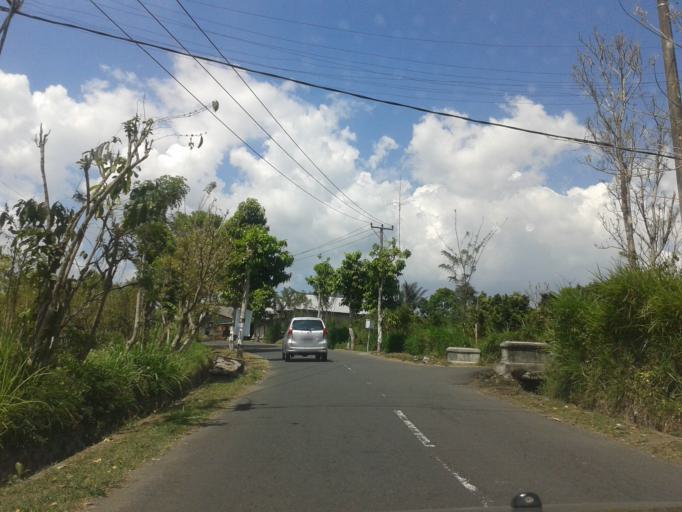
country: ID
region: Bali
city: Banjar Tiga
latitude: -8.3296
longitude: 115.3253
